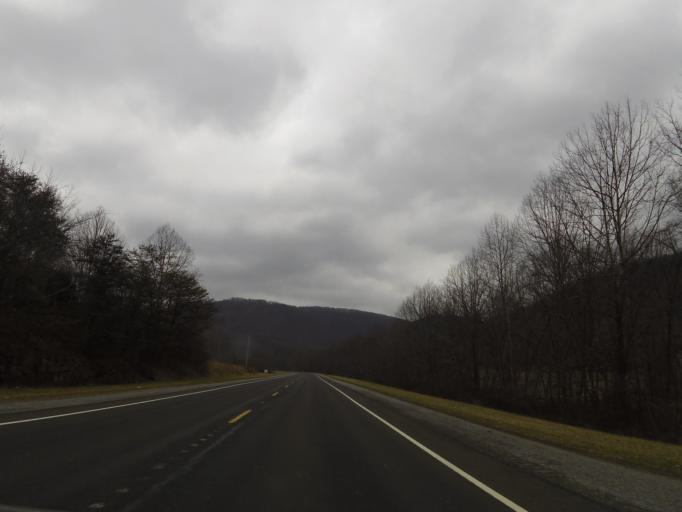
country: US
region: Tennessee
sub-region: Scott County
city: Huntsville
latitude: 36.3791
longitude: -84.3535
